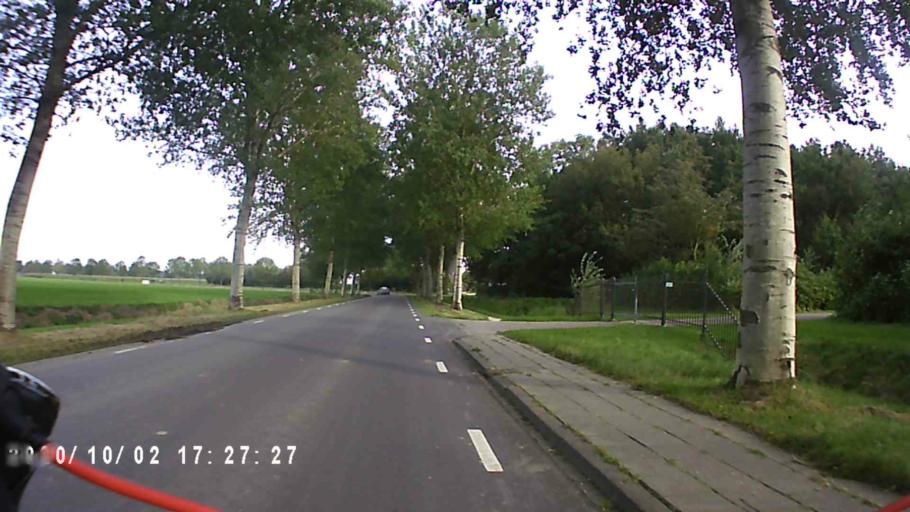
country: NL
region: Groningen
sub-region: Gemeente De Marne
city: Ulrum
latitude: 53.3363
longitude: 6.3120
